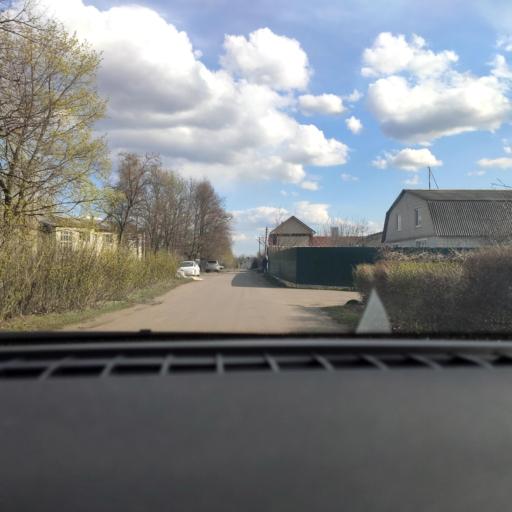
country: RU
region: Voronezj
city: Maslovka
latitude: 51.5359
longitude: 39.3320
